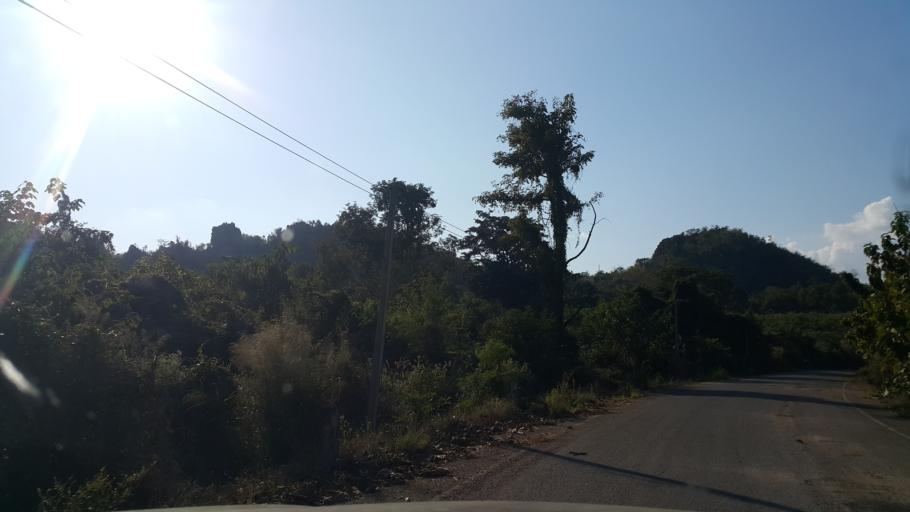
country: TH
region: Sukhothai
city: Thung Saliam
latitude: 17.3886
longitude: 99.5110
